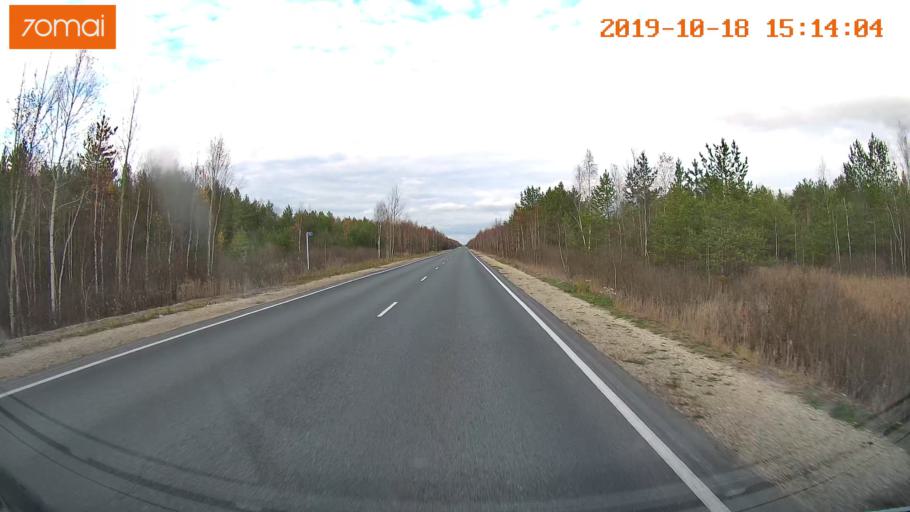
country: RU
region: Vladimir
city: Gus'-Khrustal'nyy
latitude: 55.5967
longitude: 40.7195
